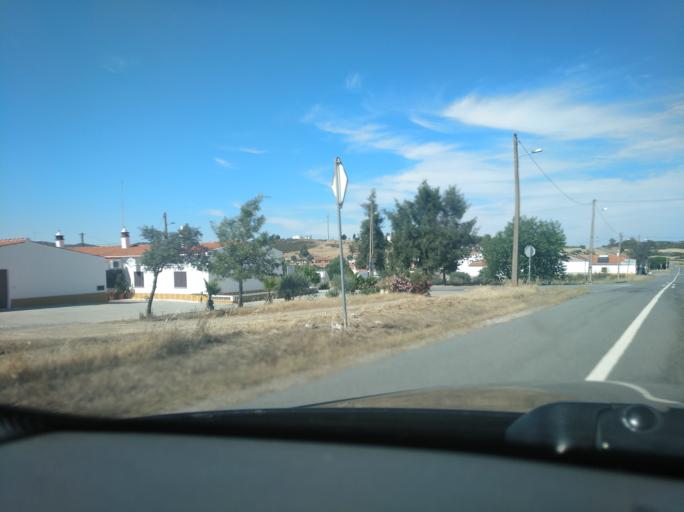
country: PT
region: Beja
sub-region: Mertola
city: Mertola
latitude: 37.6116
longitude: -7.7924
